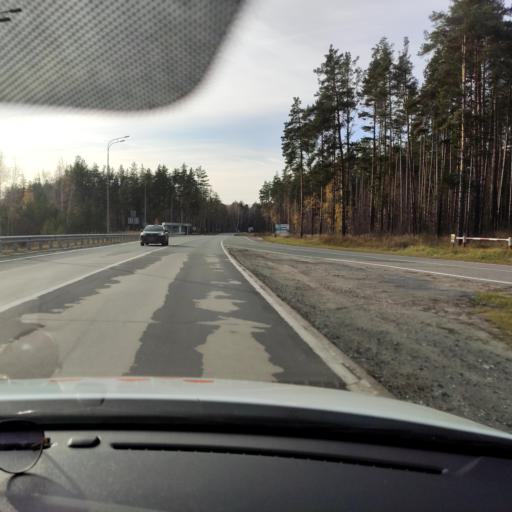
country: RU
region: Tatarstan
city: Stolbishchi
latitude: 55.6356
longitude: 49.1068
